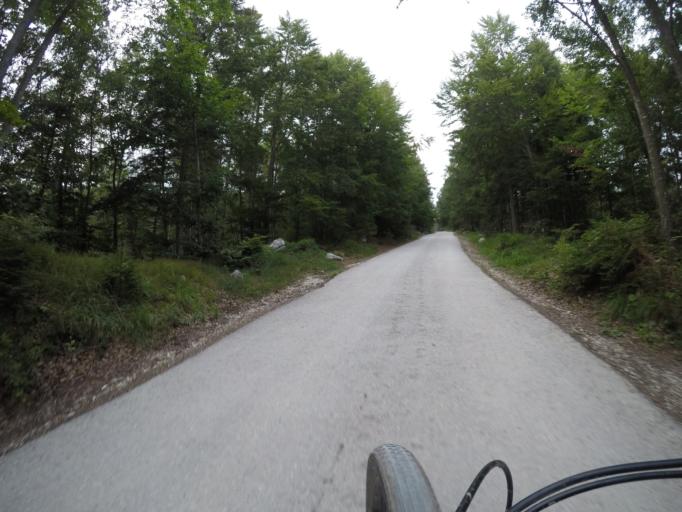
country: IT
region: Veneto
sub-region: Provincia di Vicenza
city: Gallio
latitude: 45.9080
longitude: 11.5245
